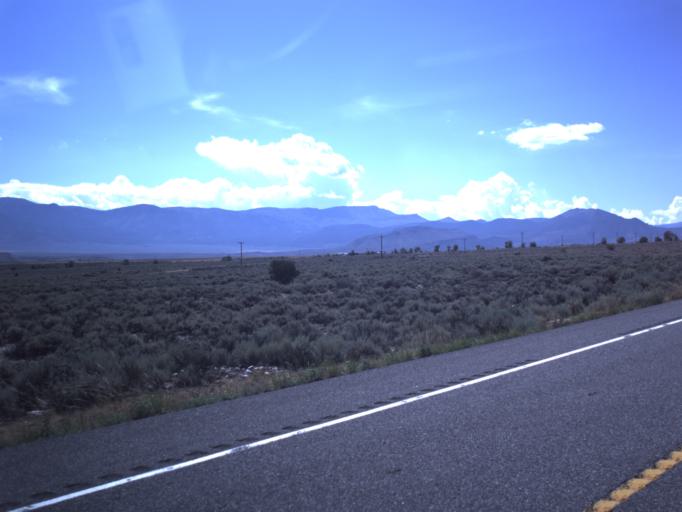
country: US
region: Utah
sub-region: Piute County
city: Junction
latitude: 38.3949
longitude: -112.2310
